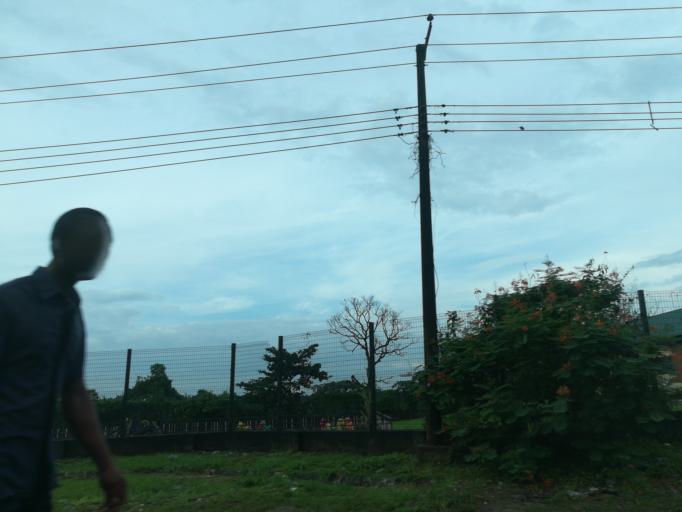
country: NG
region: Rivers
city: Port Harcourt
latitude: 4.7846
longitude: 7.0042
